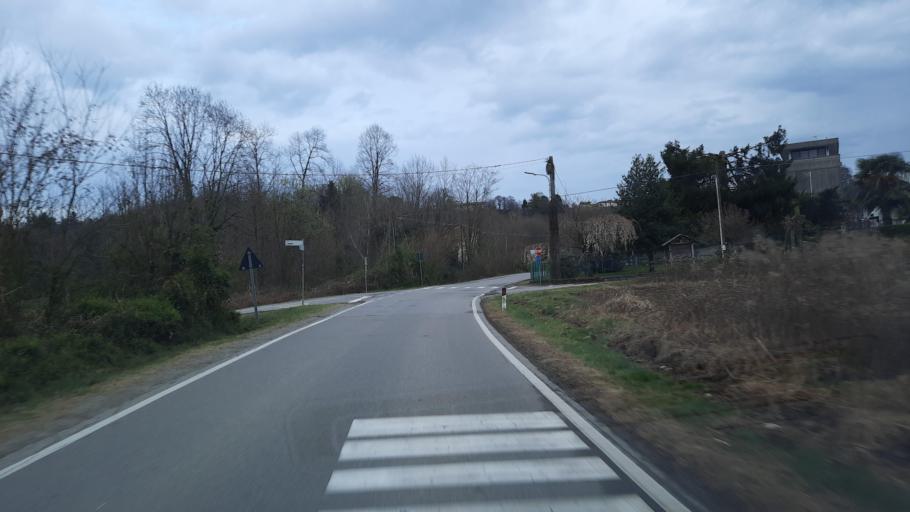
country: IT
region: Piedmont
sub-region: Provincia di Novara
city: San Maurizio D'Opaglio
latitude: 45.7834
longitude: 8.3911
